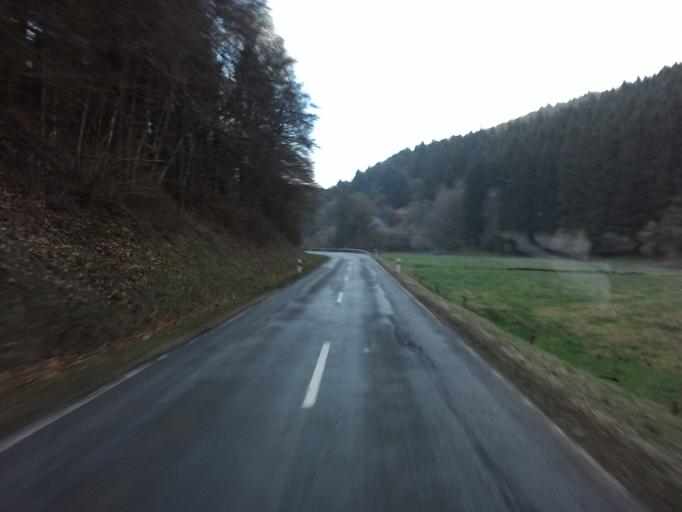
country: DE
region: Rheinland-Pfalz
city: Scheuern
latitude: 50.0272
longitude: 6.2957
